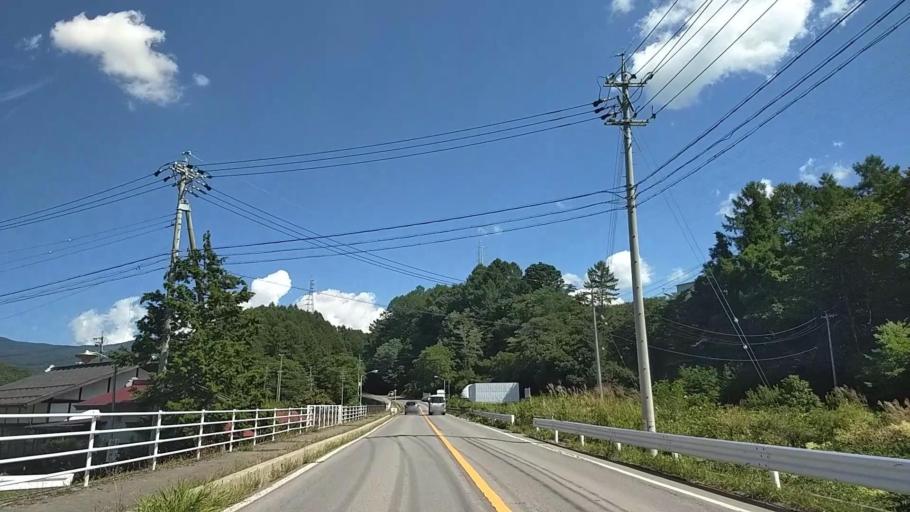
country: JP
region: Nagano
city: Chino
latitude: 36.0329
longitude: 138.2007
